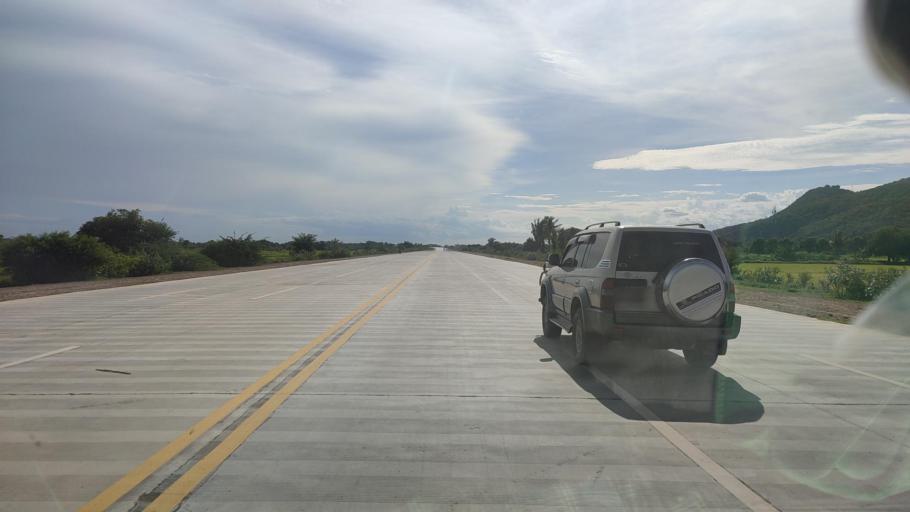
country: MM
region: Mandalay
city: Kyaukse
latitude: 21.5970
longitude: 96.1675
